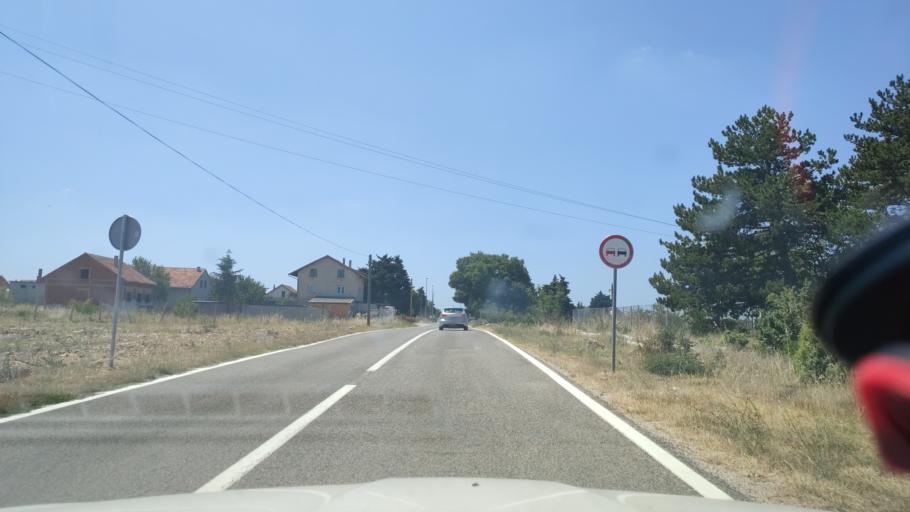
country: HR
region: Sibensko-Kniniska
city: Kistanje
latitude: 43.9862
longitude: 15.9735
